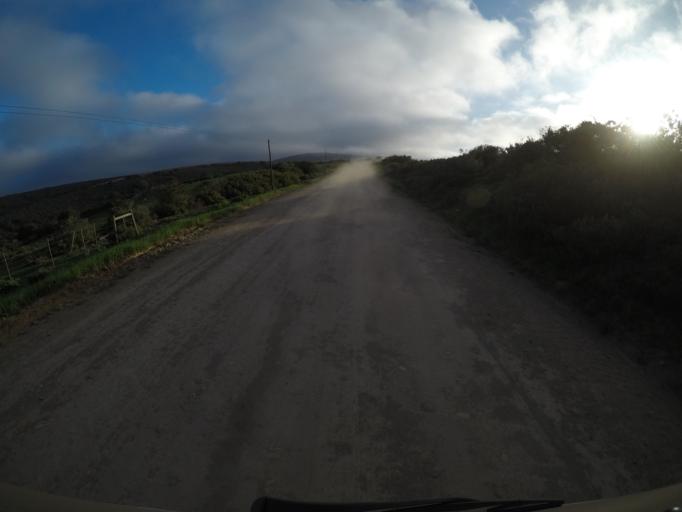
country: ZA
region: Western Cape
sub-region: Eden District Municipality
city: Mossel Bay
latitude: -34.1316
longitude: 22.0461
